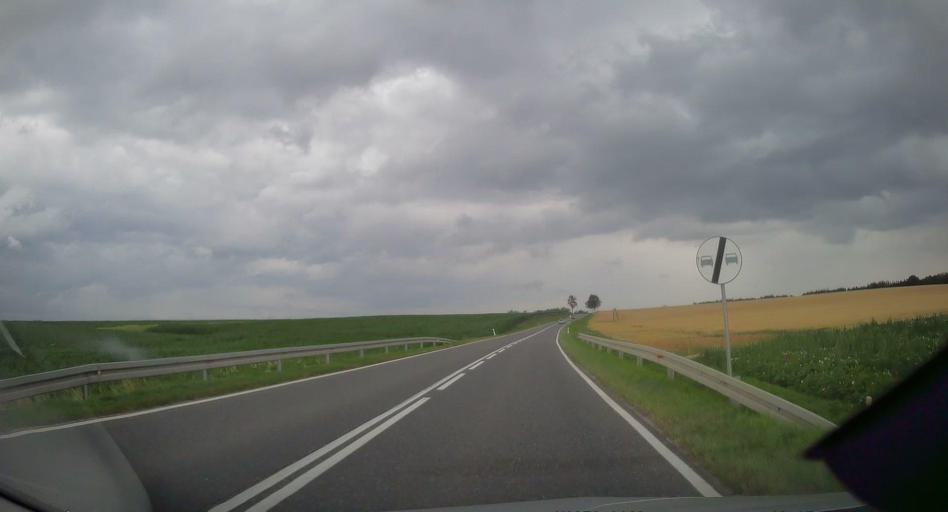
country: PL
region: Opole Voivodeship
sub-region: Powiat prudnicki
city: Moszczanka
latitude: 50.4199
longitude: 17.4699
